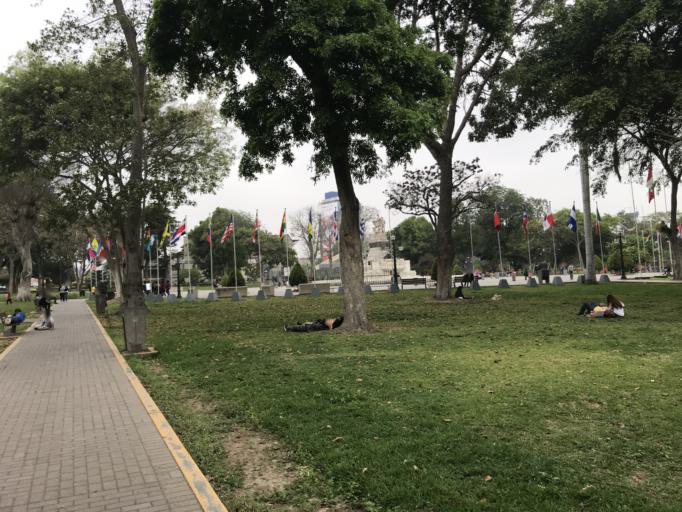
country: PE
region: Lima
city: Lima
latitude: -12.0618
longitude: -77.0372
